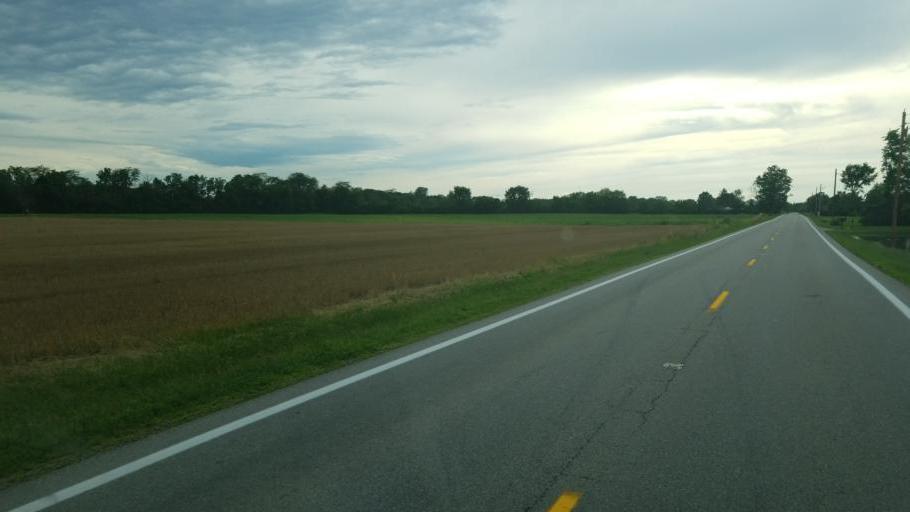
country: US
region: Ohio
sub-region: Delaware County
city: Ashley
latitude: 40.4107
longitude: -82.9907
